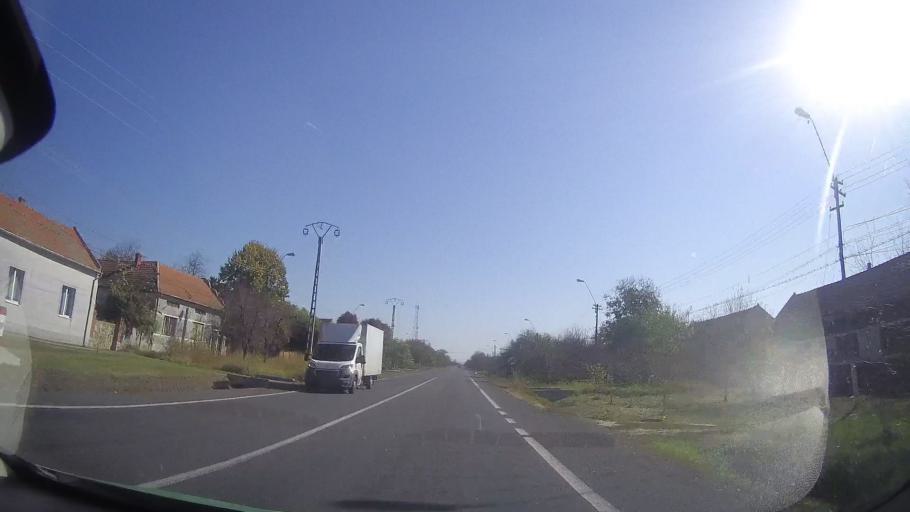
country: RO
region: Timis
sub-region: Comuna Belint
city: Belint
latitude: 45.7486
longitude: 21.7708
